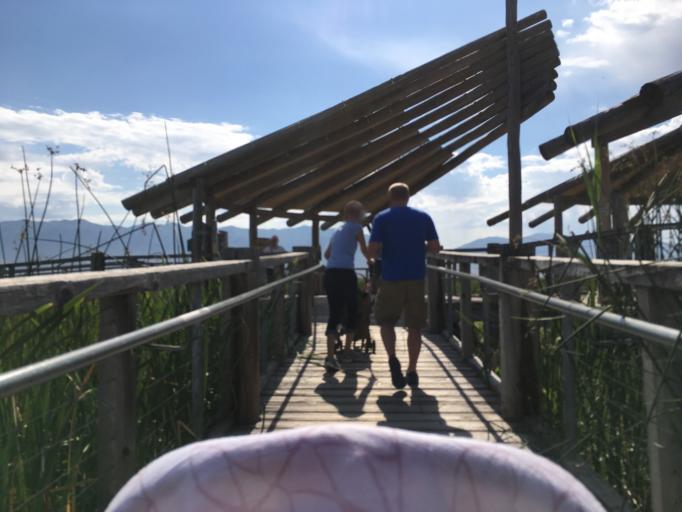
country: US
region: Utah
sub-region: Davis County
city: Layton
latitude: 41.0403
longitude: -112.0258
